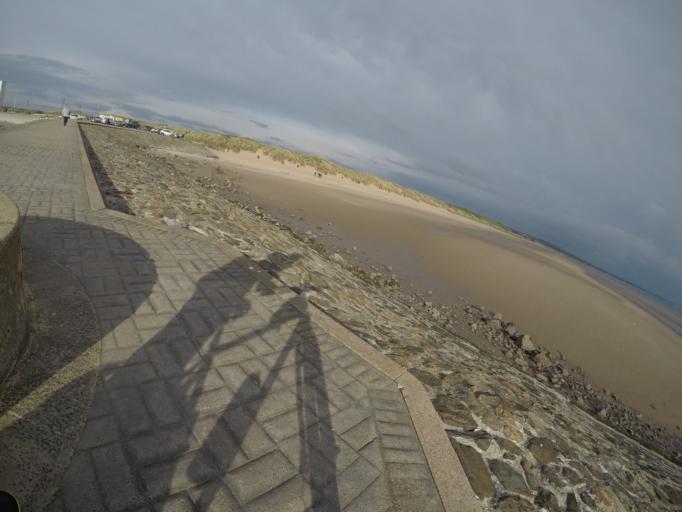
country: GB
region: Scotland
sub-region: North Ayrshire
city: Irvine
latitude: 55.6042
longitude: -4.6955
